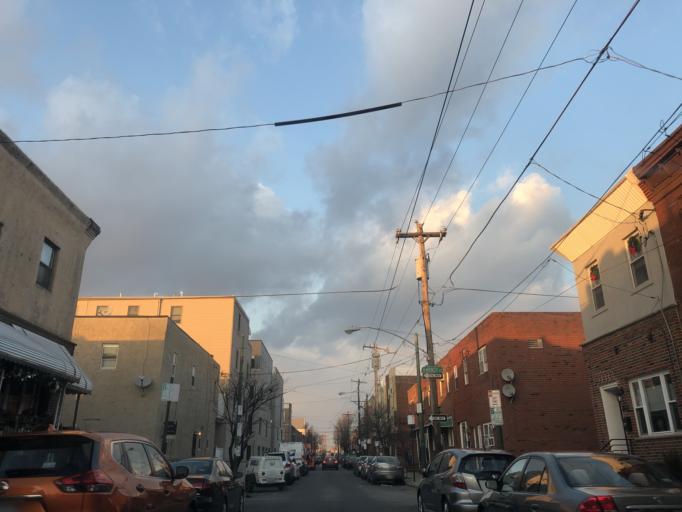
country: US
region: Pennsylvania
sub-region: Philadelphia County
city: Philadelphia
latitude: 39.9240
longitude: -75.1644
